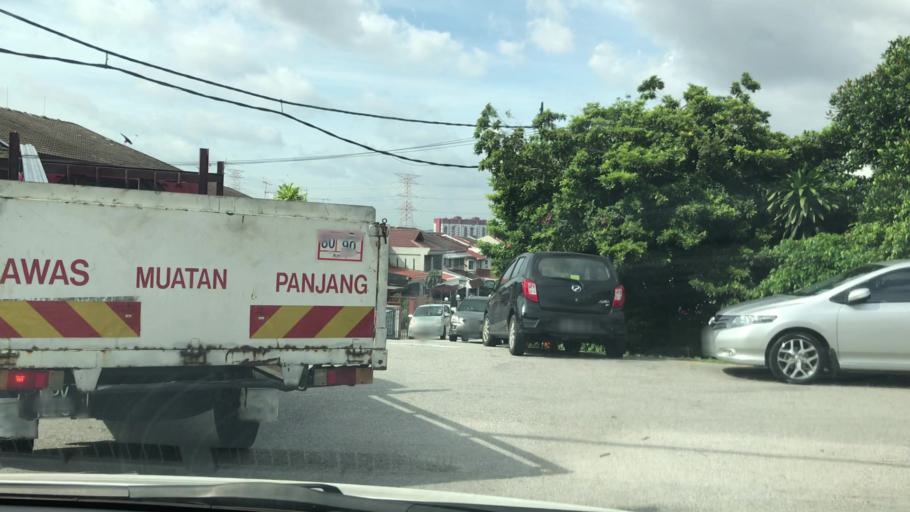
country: MY
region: Selangor
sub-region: Petaling
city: Petaling Jaya
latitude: 3.1083
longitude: 101.6222
